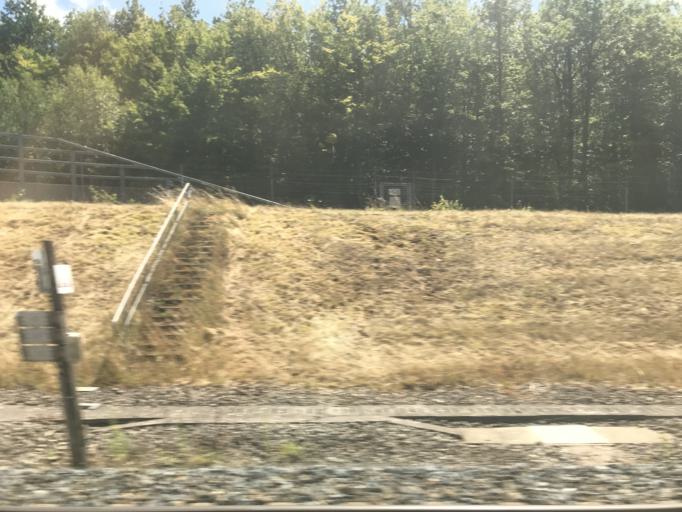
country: FR
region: Lorraine
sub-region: Departement de la Moselle
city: Solgne
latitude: 48.9600
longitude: 6.3169
